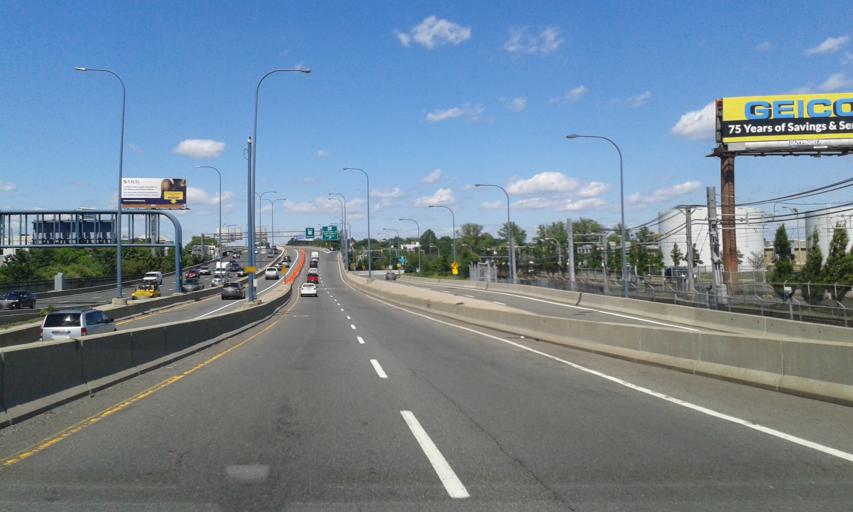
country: US
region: Massachusetts
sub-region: Suffolk County
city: Chelsea
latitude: 42.3766
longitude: -71.0280
